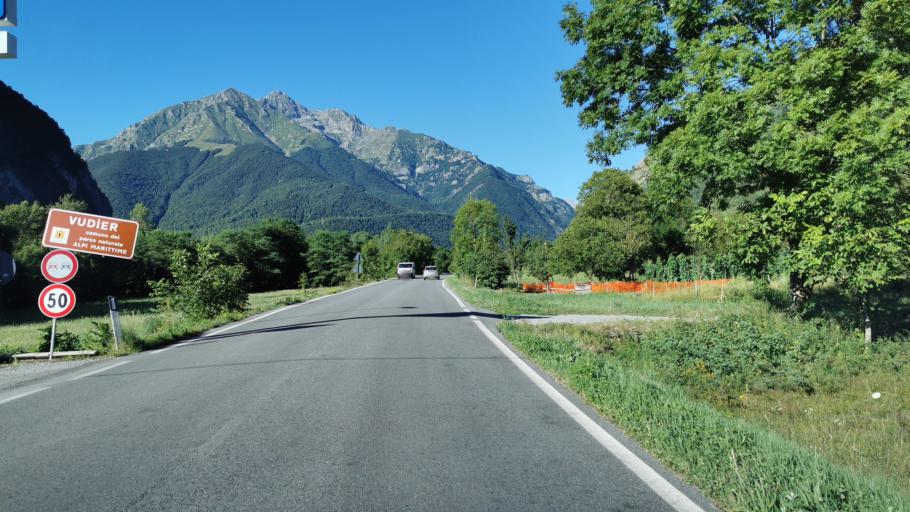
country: IT
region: Piedmont
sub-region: Provincia di Cuneo
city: Valdieri
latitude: 44.2724
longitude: 7.3958
